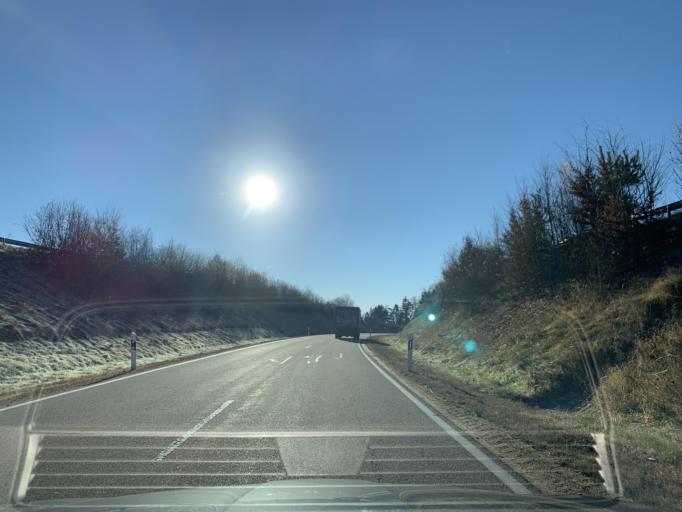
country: DE
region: Bavaria
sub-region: Upper Palatinate
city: Oberviechtach
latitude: 49.4382
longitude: 12.4181
